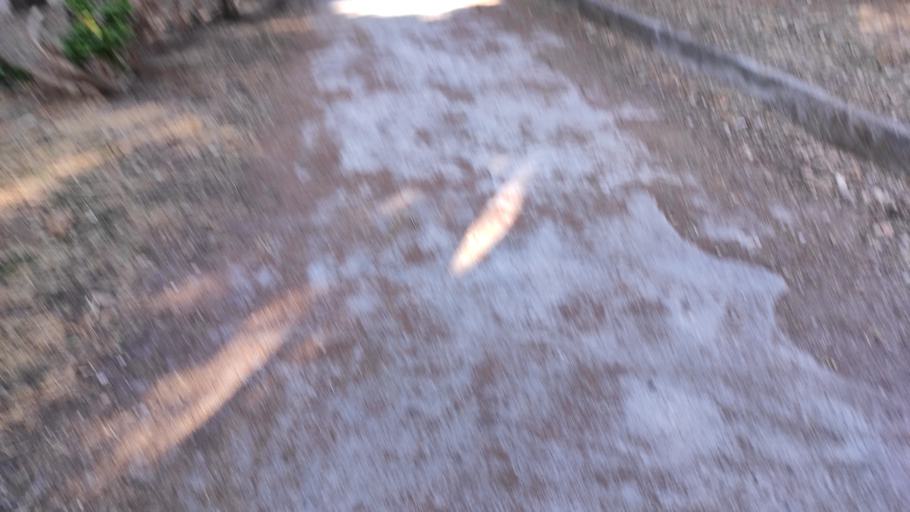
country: GR
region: South Aegean
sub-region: Nomos Dodekanisou
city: Rodos
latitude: 36.4397
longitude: 28.2300
